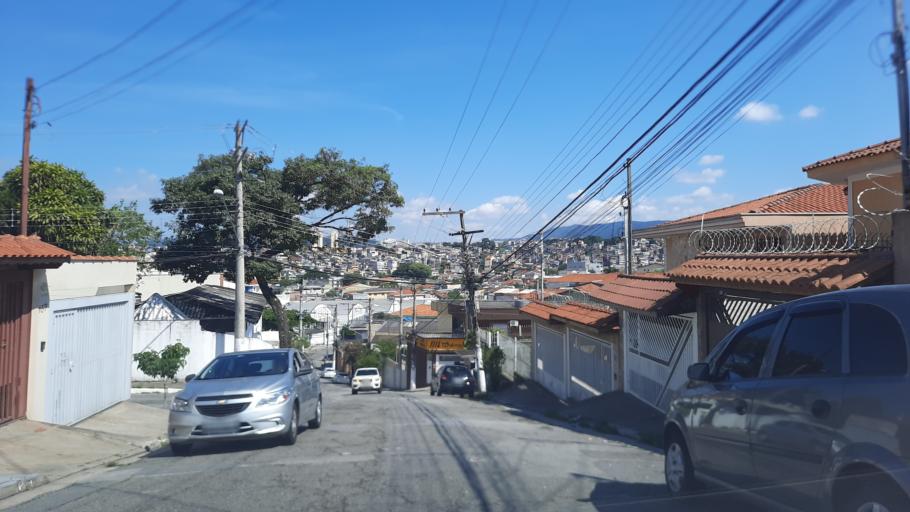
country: BR
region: Sao Paulo
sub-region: Sao Paulo
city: Sao Paulo
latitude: -23.4915
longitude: -46.6788
